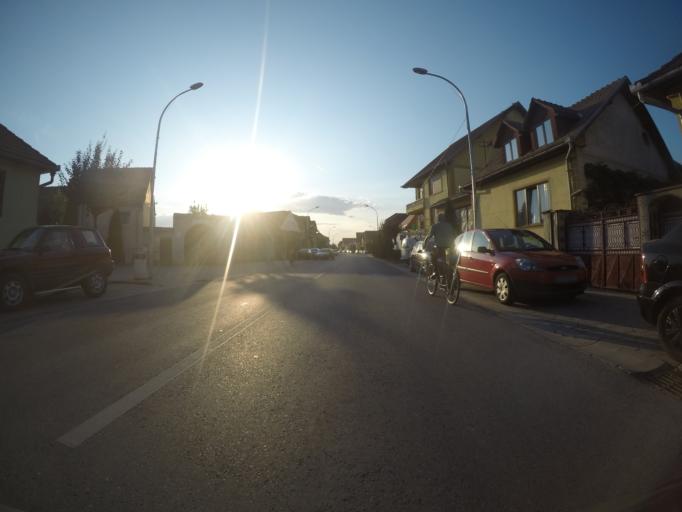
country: RO
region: Sibiu
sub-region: Comuna Selimbar
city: Selimbar
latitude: 45.7678
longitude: 24.1944
